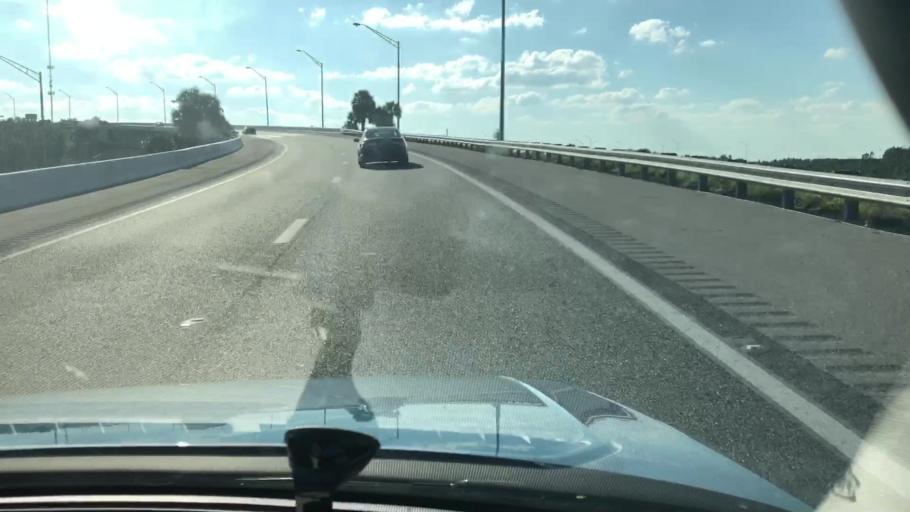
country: US
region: Florida
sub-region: Orange County
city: Paradise Heights
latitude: 28.6530
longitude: -81.5395
